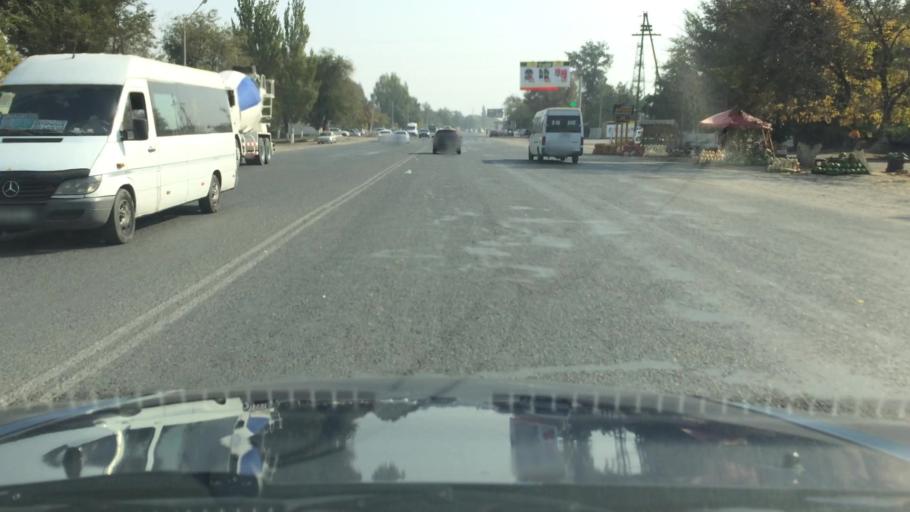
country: KG
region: Chuy
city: Lebedinovka
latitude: 42.8880
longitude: 74.6632
